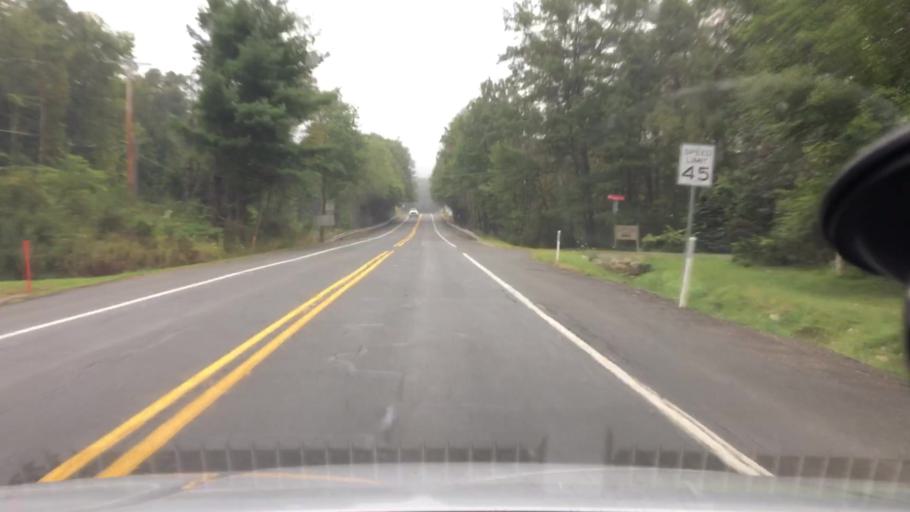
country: US
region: Pennsylvania
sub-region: Monroe County
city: Mountainhome
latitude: 41.1410
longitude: -75.2884
